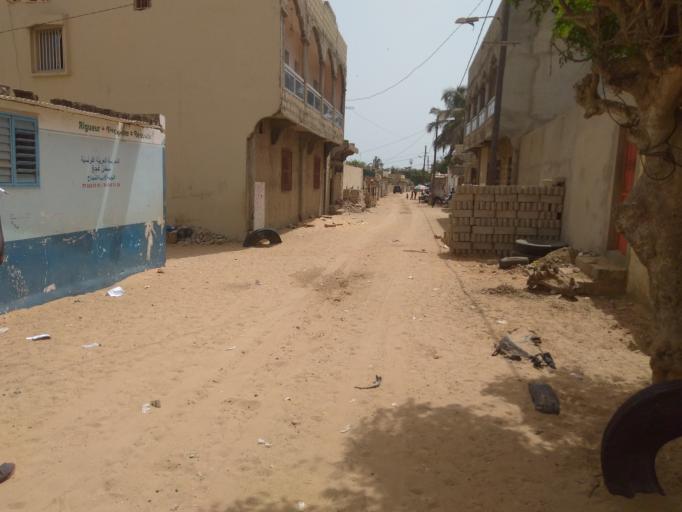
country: SN
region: Dakar
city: Pikine
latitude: 14.7918
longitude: -17.3383
